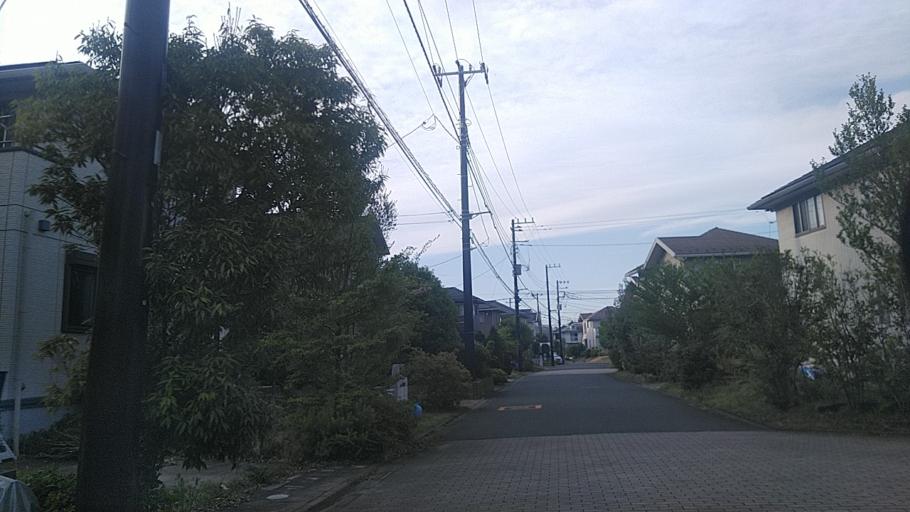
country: JP
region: Chiba
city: Shiroi
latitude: 35.7920
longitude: 140.1366
